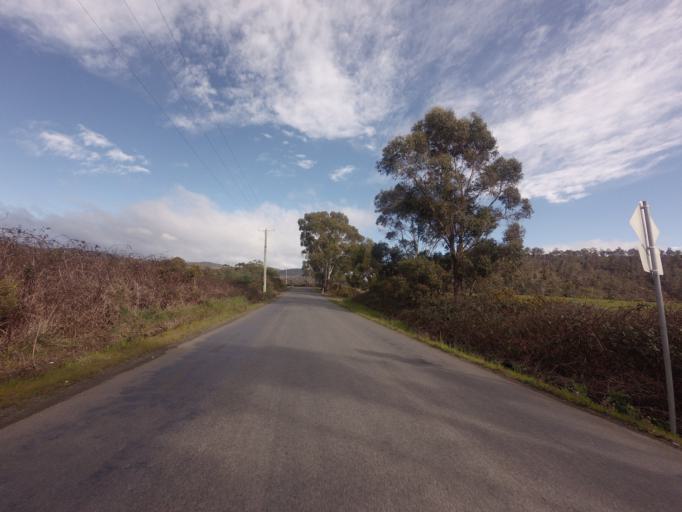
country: AU
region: Tasmania
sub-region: Derwent Valley
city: New Norfolk
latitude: -42.7784
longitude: 147.0186
